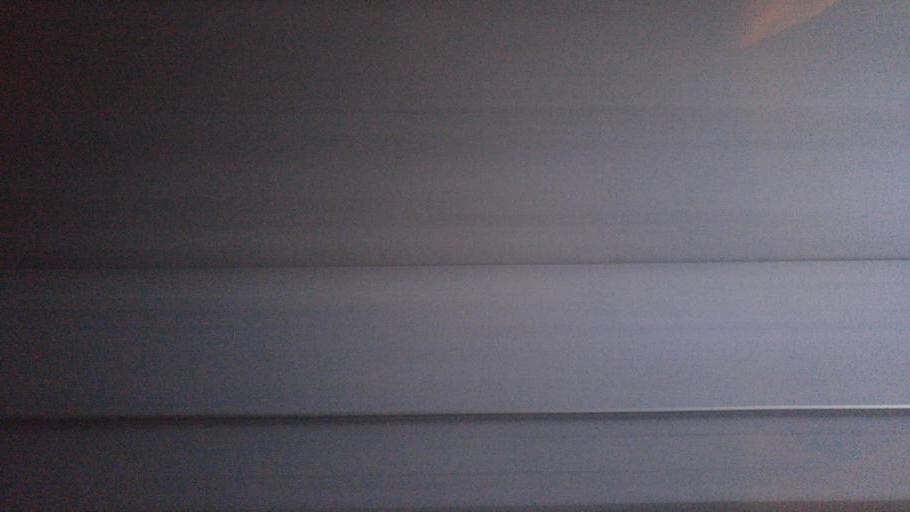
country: NO
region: Akershus
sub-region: Sorum
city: Frogner
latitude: 60.0154
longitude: 11.1125
